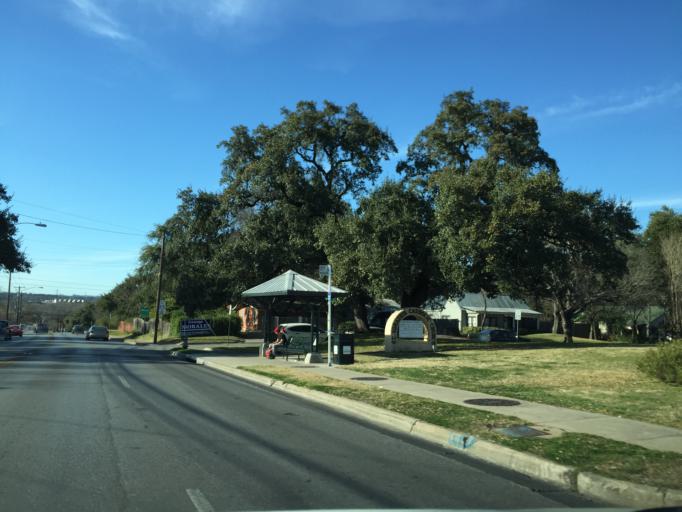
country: US
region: Texas
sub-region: Travis County
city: Austin
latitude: 30.2400
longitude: -97.7553
